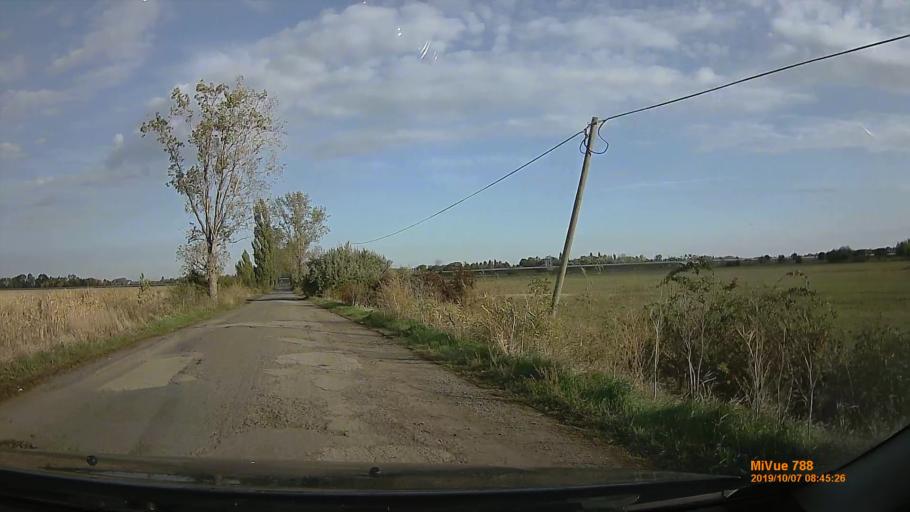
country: HU
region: Bekes
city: Szarvas
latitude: 46.8137
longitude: 20.5265
